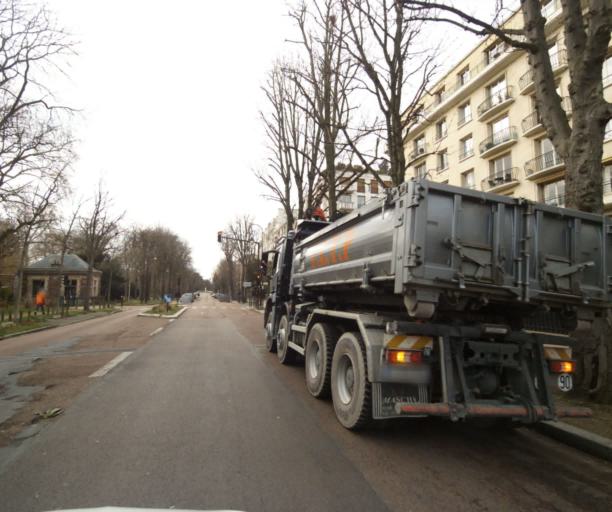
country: FR
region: Ile-de-France
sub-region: Departement des Hauts-de-Seine
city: Neuilly-sur-Seine
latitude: 48.8772
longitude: 2.2567
